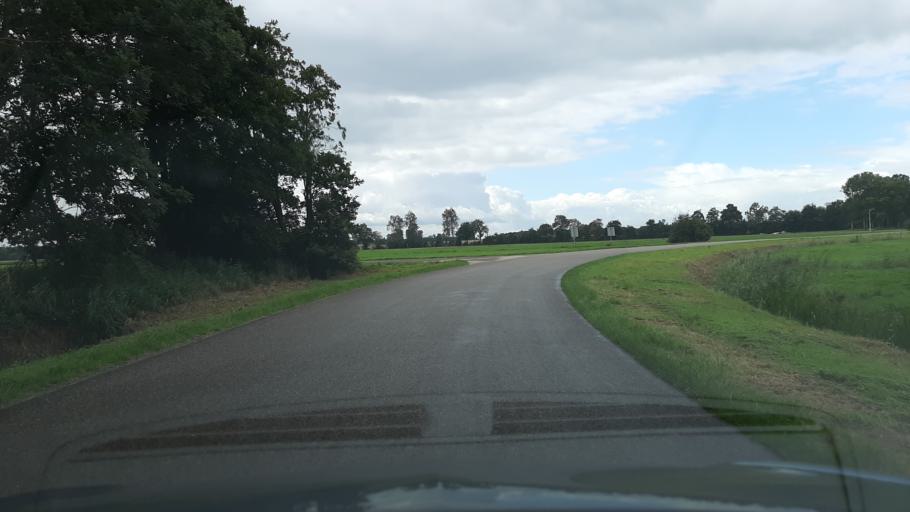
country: NL
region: Friesland
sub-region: Gemeente Weststellingwerf
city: Wolvega
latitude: 52.9139
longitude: 6.0108
